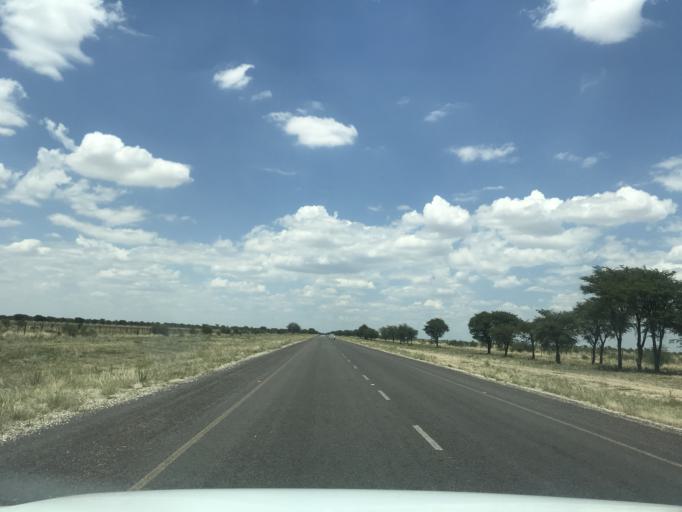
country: BW
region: South East
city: Janeng
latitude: -25.5965
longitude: 25.1658
